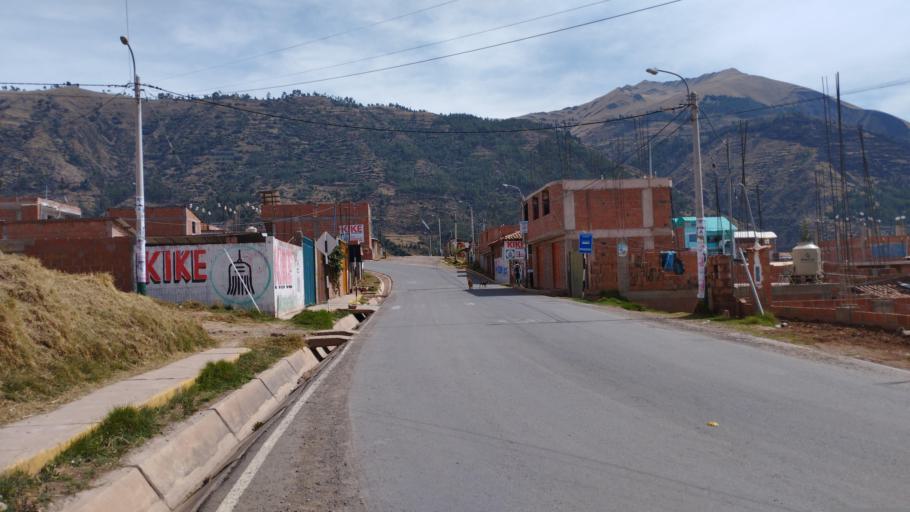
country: PE
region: Cusco
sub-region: Provincia de Cusco
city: Cusco
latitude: -13.5208
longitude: -71.9146
